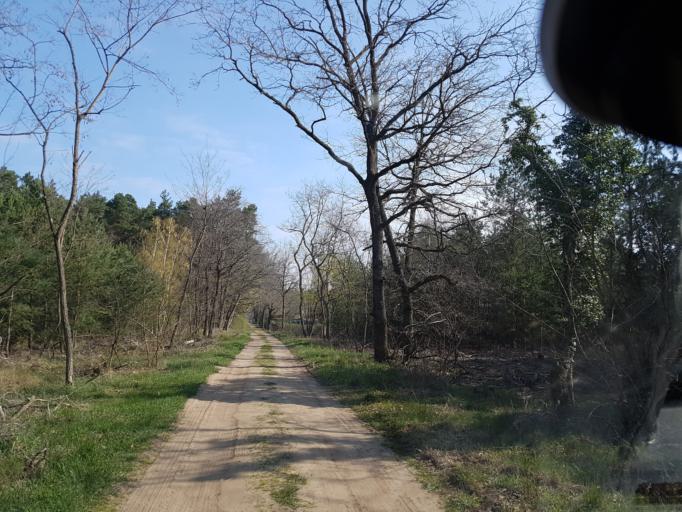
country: DE
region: Brandenburg
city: Bruck
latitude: 52.1657
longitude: 12.7238
